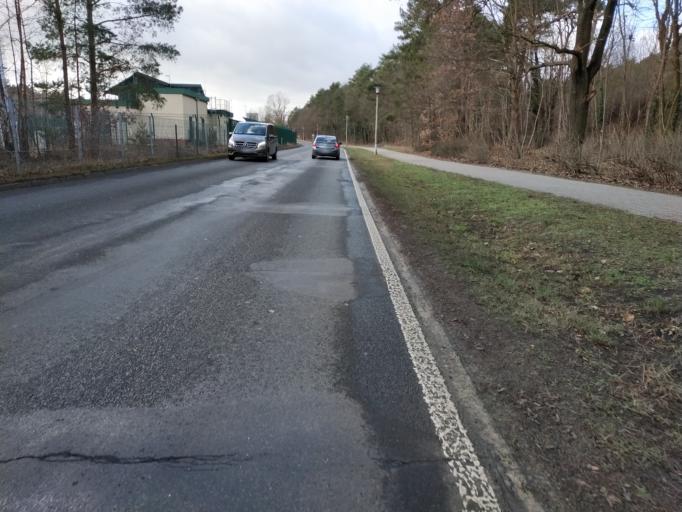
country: DE
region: Brandenburg
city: Petershagen
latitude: 52.5326
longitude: 13.8308
